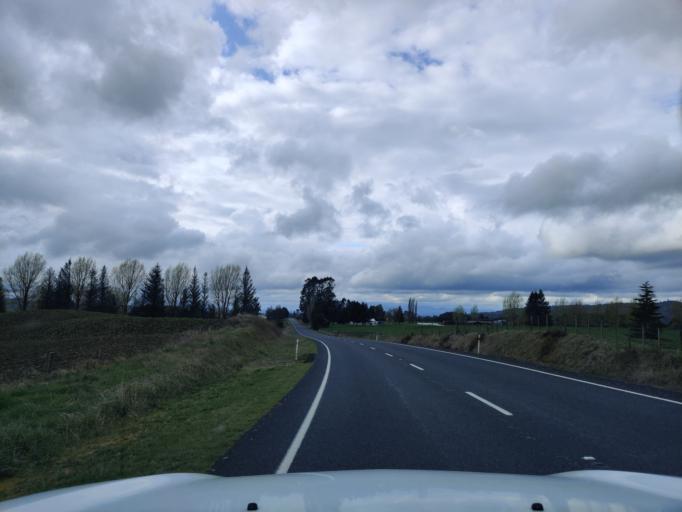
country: NZ
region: Waikato
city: Turangi
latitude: -39.0500
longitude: 175.3836
